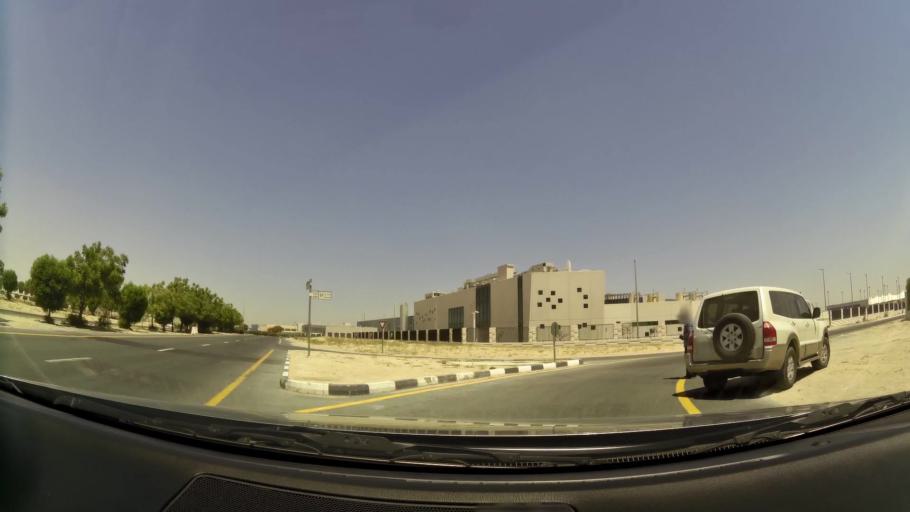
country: AE
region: Dubai
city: Dubai
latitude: 24.9736
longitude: 55.1987
